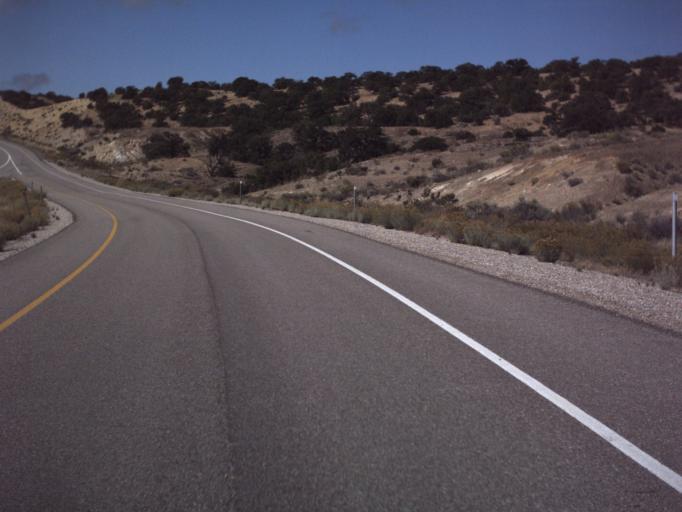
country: US
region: Utah
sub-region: Emery County
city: Ferron
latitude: 38.8566
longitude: -110.9166
